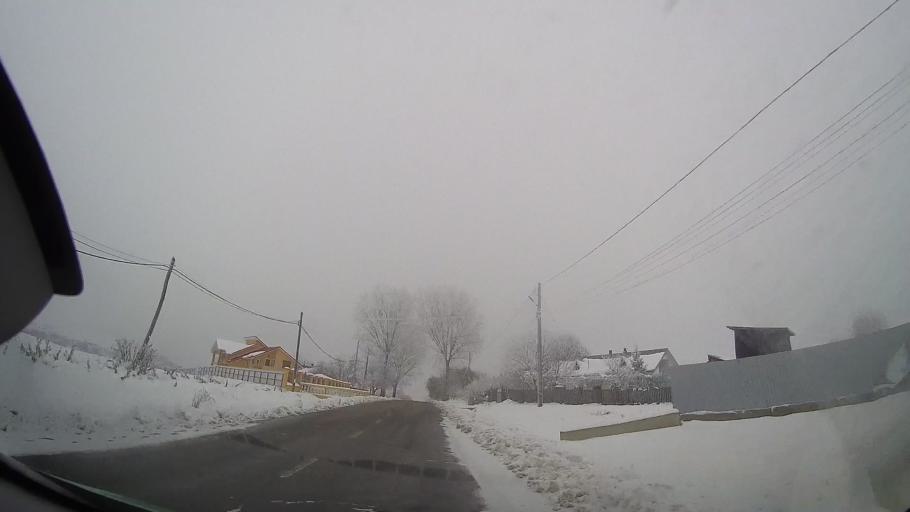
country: RO
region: Neamt
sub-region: Comuna Icusesti
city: Balusesti
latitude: 46.8667
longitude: 26.9972
